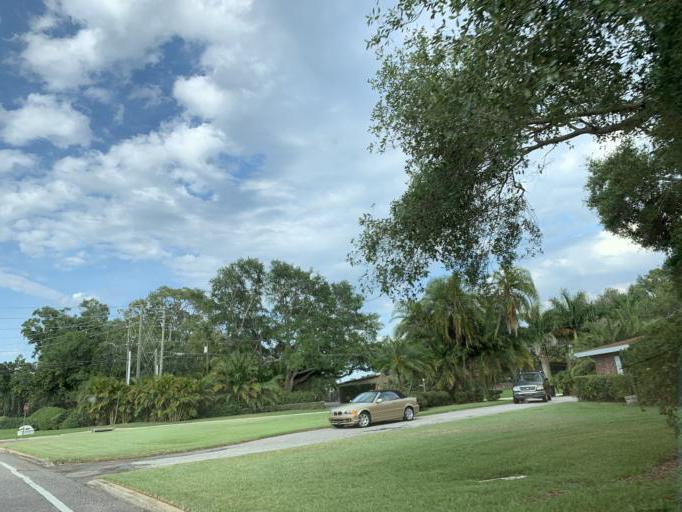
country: US
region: Florida
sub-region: Pinellas County
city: Saint Petersburg
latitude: 27.7950
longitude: -82.6121
